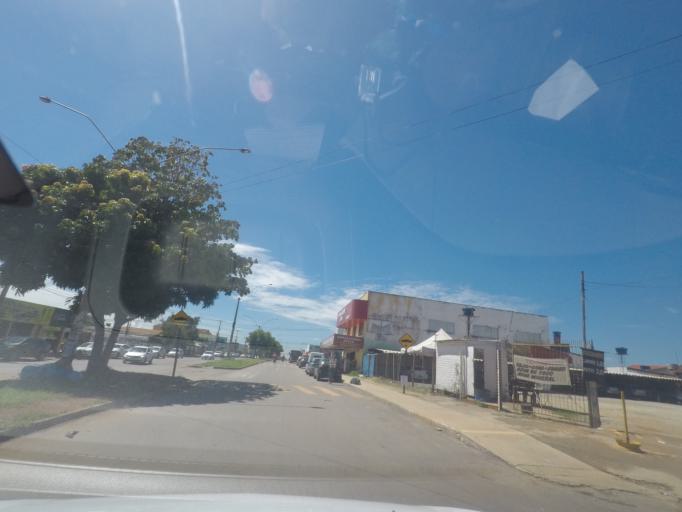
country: BR
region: Goias
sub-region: Aparecida De Goiania
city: Aparecida de Goiania
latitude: -16.7672
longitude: -49.3465
